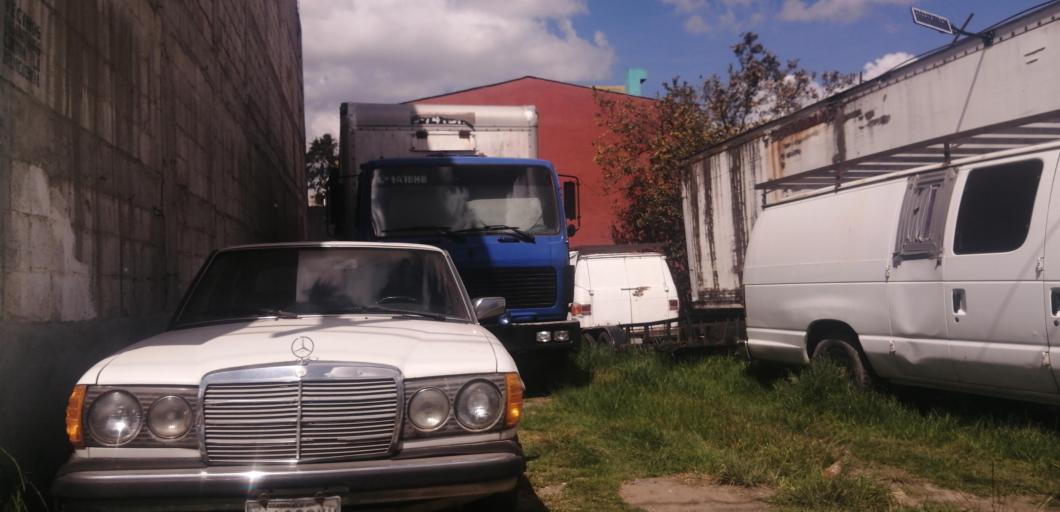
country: GT
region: Quetzaltenango
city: Quetzaltenango
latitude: 14.8349
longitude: -91.5301
